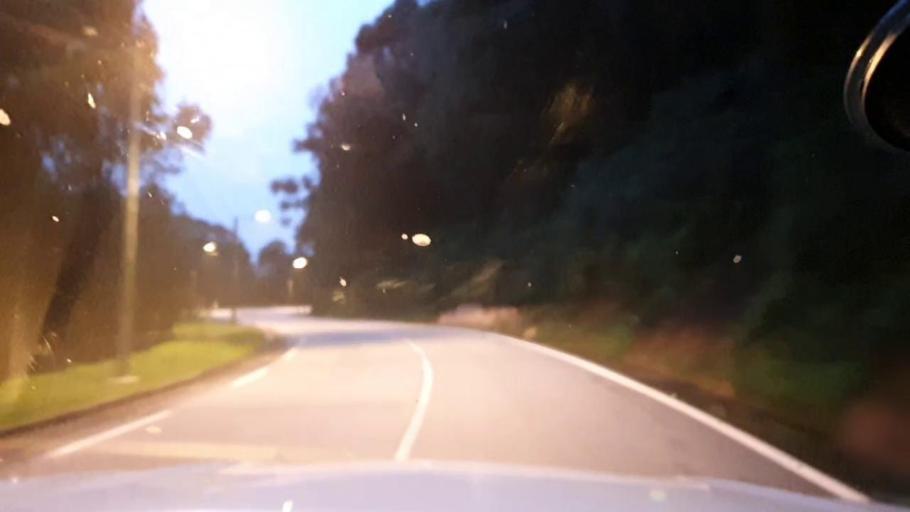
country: RW
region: Southern Province
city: Nzega
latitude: -2.5310
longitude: 29.3857
